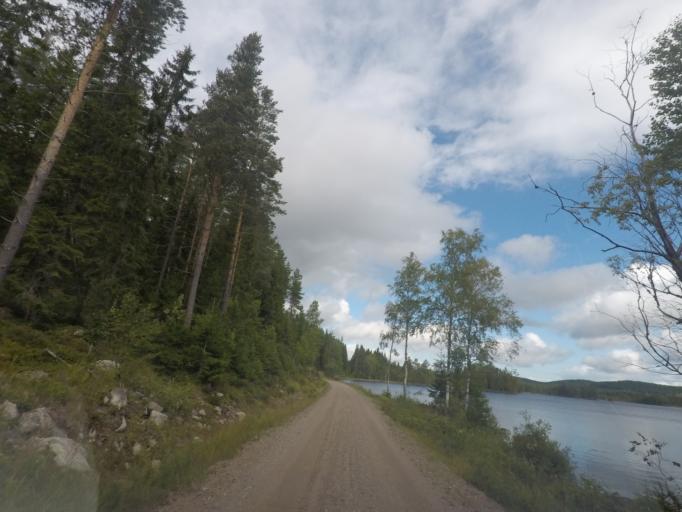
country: SE
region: Vaermland
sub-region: Filipstads Kommun
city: Lesjofors
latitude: 60.0614
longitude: 14.4379
